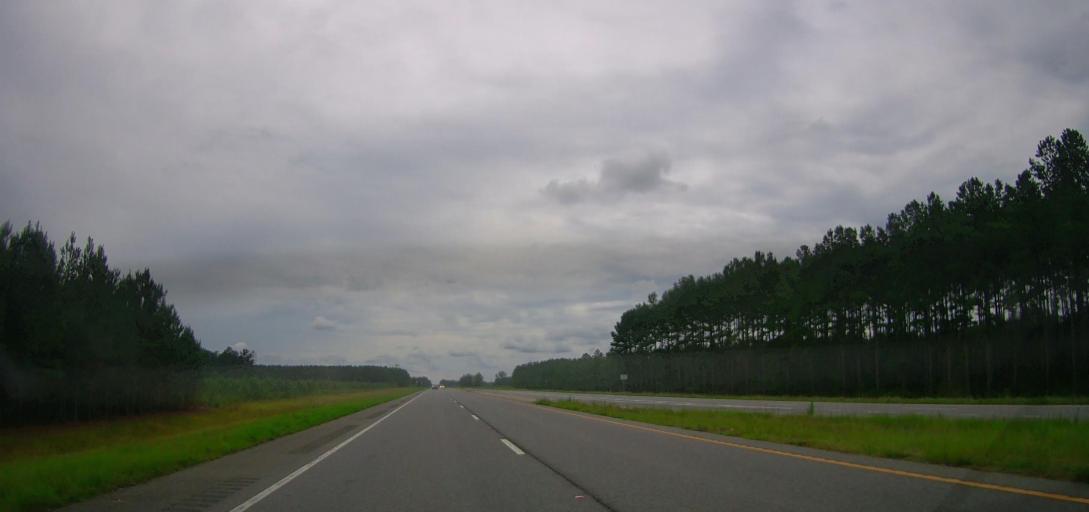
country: US
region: Georgia
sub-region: Appling County
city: Baxley
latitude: 31.7522
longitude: -82.2730
